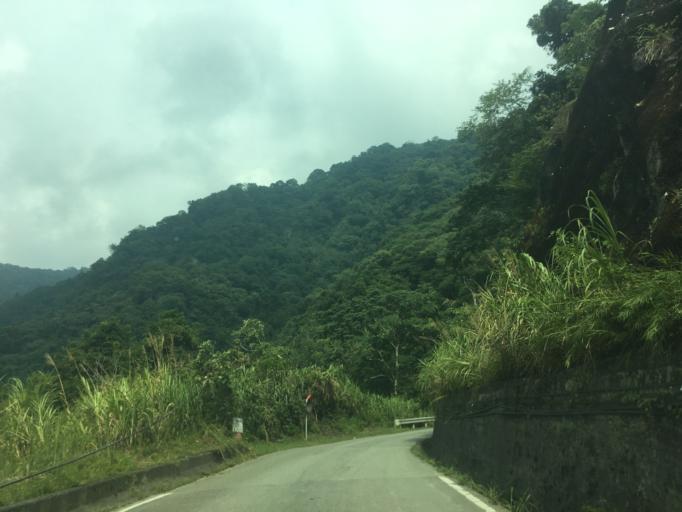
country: TW
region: Taiwan
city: Fengyuan
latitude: 24.3425
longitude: 120.9383
